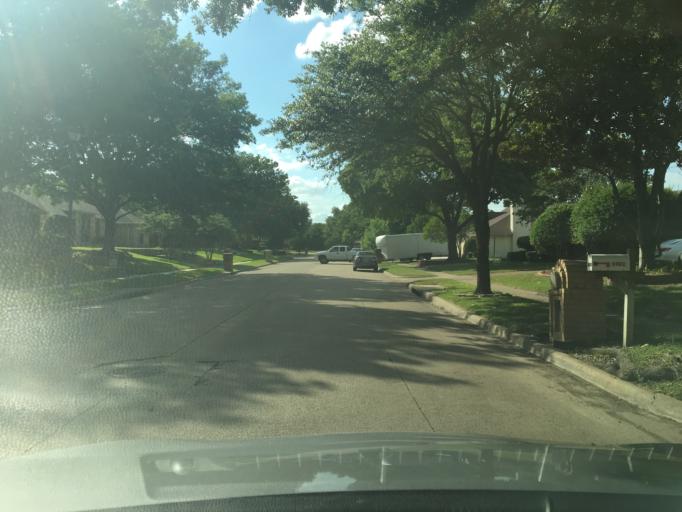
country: US
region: Texas
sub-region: Dallas County
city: Garland
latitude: 32.9392
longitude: -96.6774
